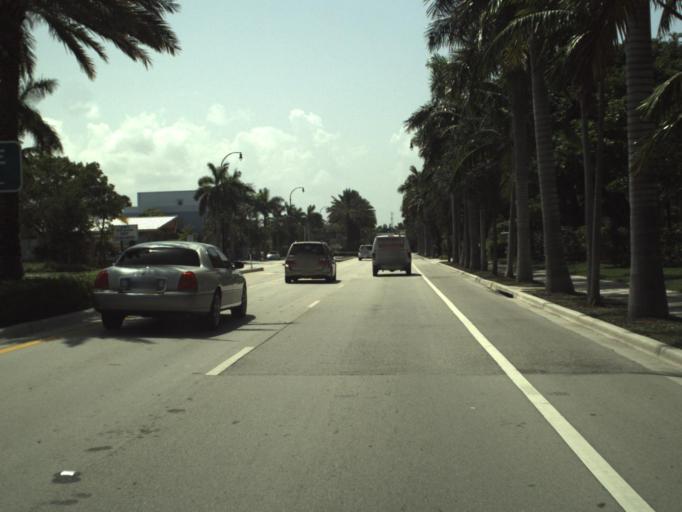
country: US
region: Florida
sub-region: Broward County
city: Deerfield Beach
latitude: 26.3149
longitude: -80.0847
